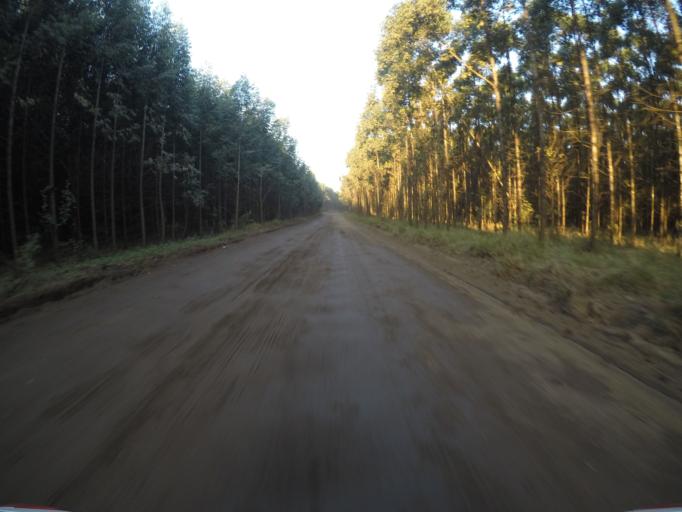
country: ZA
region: KwaZulu-Natal
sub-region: uThungulu District Municipality
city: KwaMbonambi
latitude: -28.6704
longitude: 32.0836
